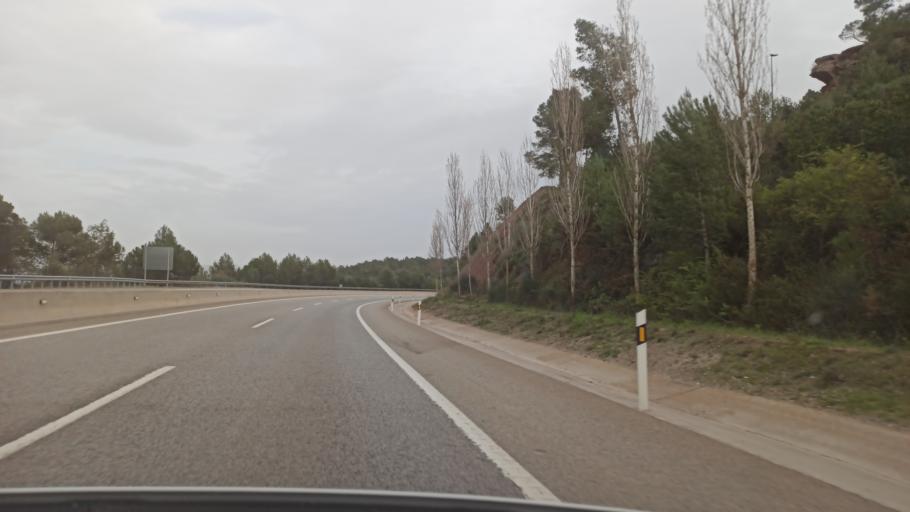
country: ES
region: Catalonia
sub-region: Provincia de Barcelona
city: Cervello
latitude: 41.3921
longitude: 1.9544
